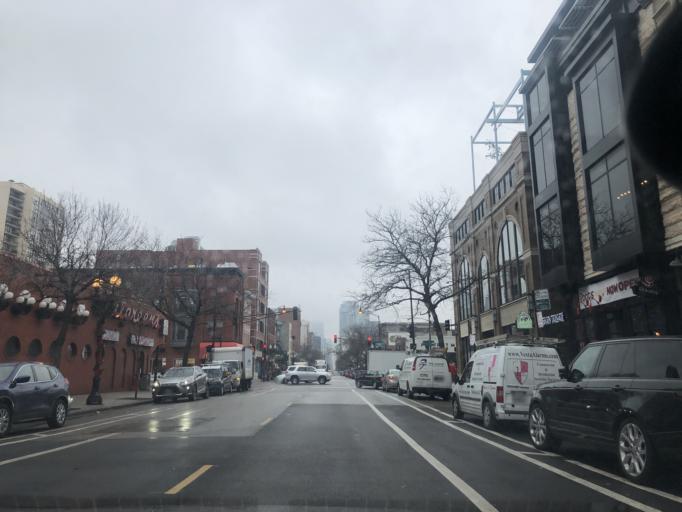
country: US
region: Illinois
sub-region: Cook County
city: Chicago
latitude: 41.9118
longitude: -87.6347
